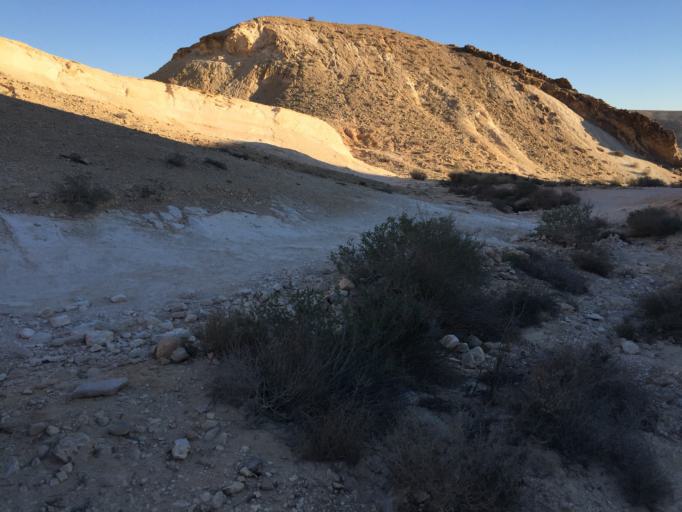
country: IL
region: Southern District
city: Midreshet Ben-Gurion
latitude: 30.8464
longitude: 34.7559
